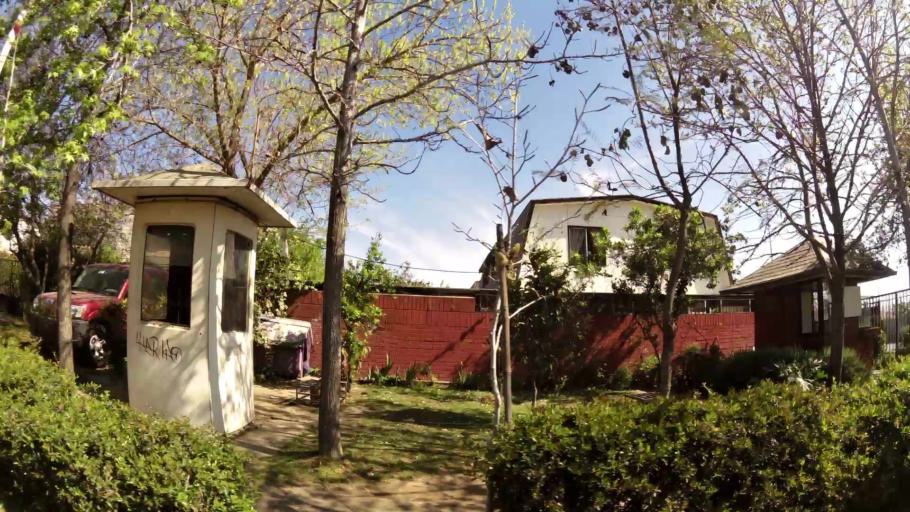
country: CL
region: Santiago Metropolitan
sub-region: Provincia de Santiago
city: Villa Presidente Frei, Nunoa, Santiago, Chile
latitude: -33.4930
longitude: -70.5822
